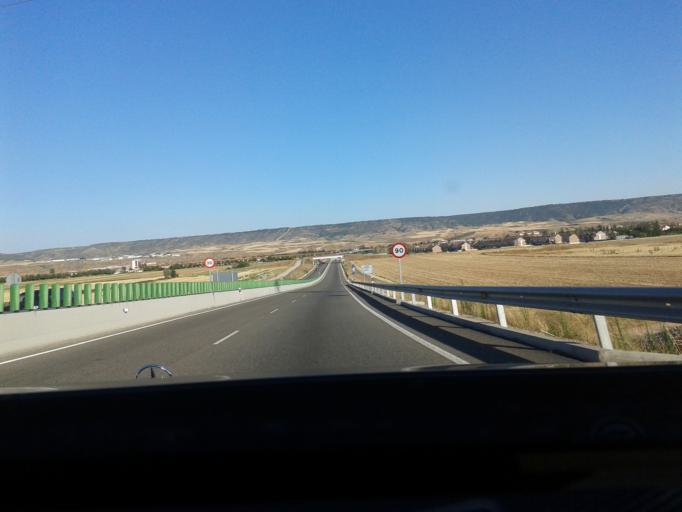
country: ES
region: Castille-La Mancha
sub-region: Provincia de Guadalajara
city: Quer
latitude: 40.5857
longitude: -3.2711
